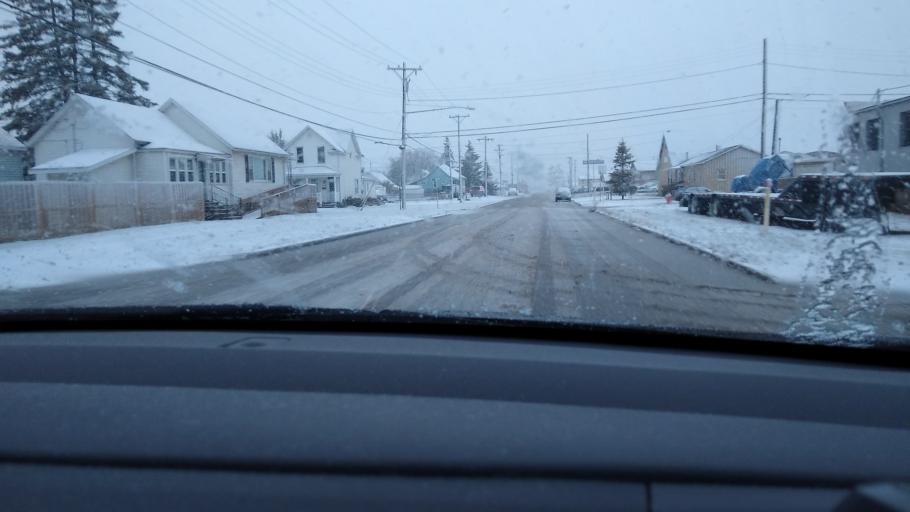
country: US
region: Michigan
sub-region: Delta County
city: Escanaba
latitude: 45.7536
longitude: -87.0725
